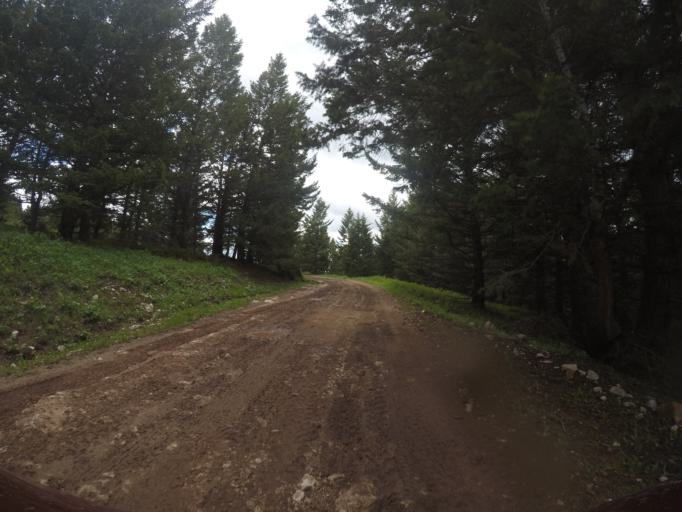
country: US
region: Wyoming
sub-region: Big Horn County
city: Lovell
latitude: 45.1726
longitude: -108.4339
